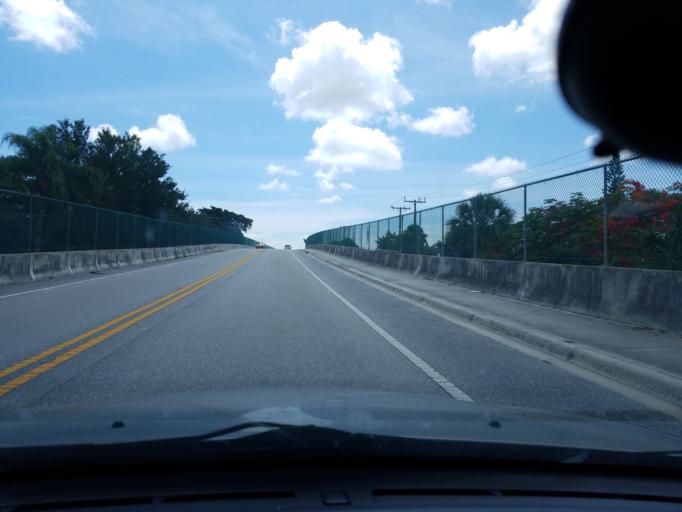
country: US
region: Florida
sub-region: Palm Beach County
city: North Palm Beach
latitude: 26.7979
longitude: -80.1006
